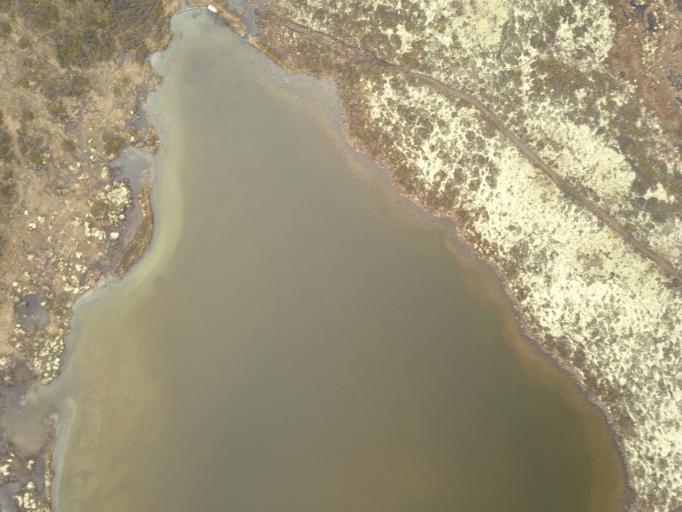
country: NO
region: Hedmark
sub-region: Folldal
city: Folldal
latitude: 62.2293
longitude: 9.6464
